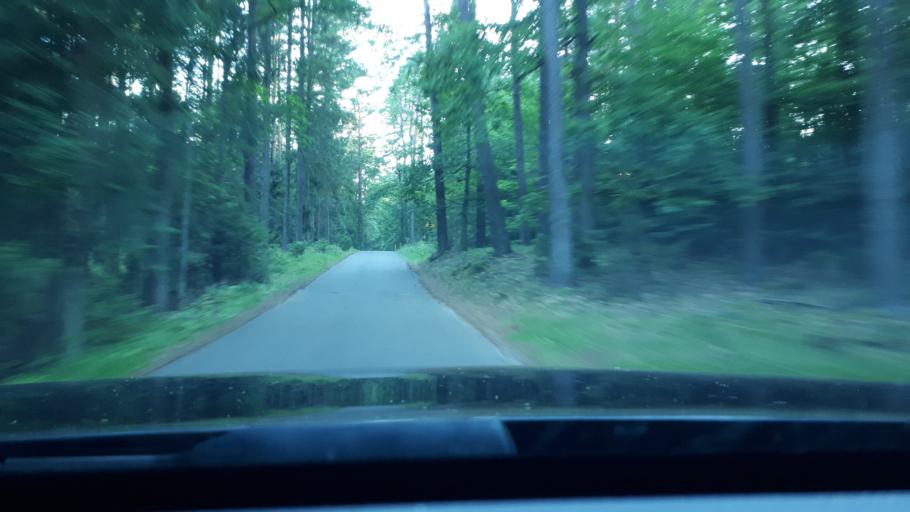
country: PL
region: Warmian-Masurian Voivodeship
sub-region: Powiat olsztynski
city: Stawiguda
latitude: 53.5885
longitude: 20.4518
